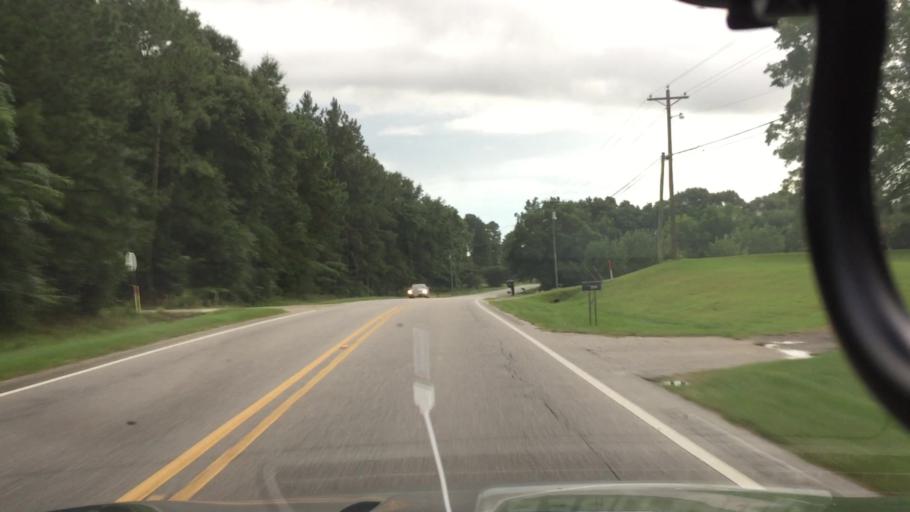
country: US
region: Alabama
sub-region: Pike County
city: Troy
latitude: 31.7285
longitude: -85.9579
